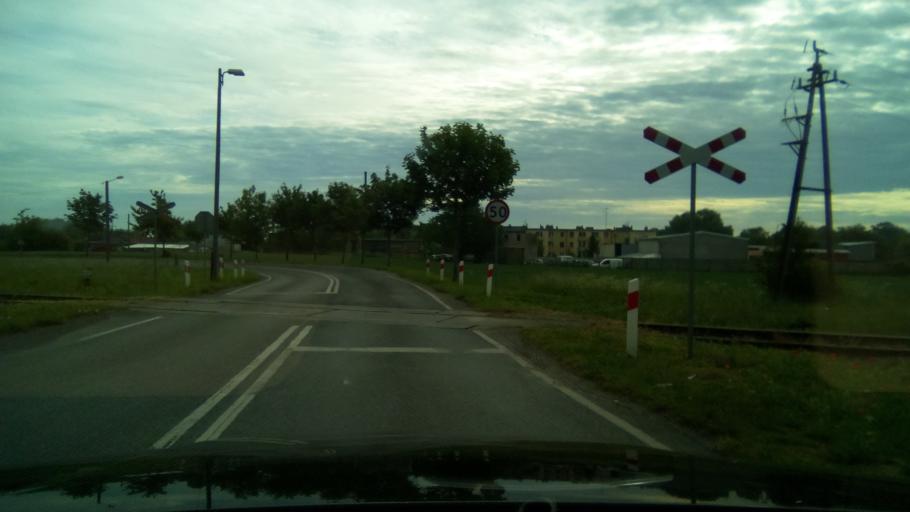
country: PL
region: Kujawsko-Pomorskie
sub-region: Powiat zninski
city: Janowiec Wielkopolski
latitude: 52.7470
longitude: 17.4877
